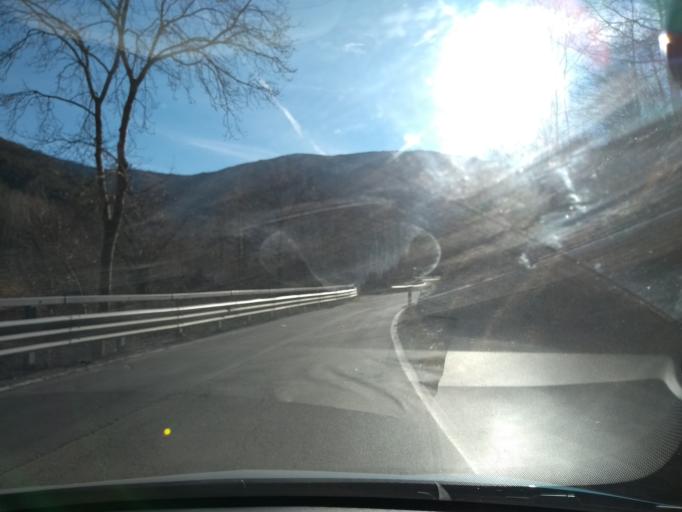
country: IT
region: Piedmont
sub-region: Provincia di Torino
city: La Villa
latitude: 45.2440
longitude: 7.4337
